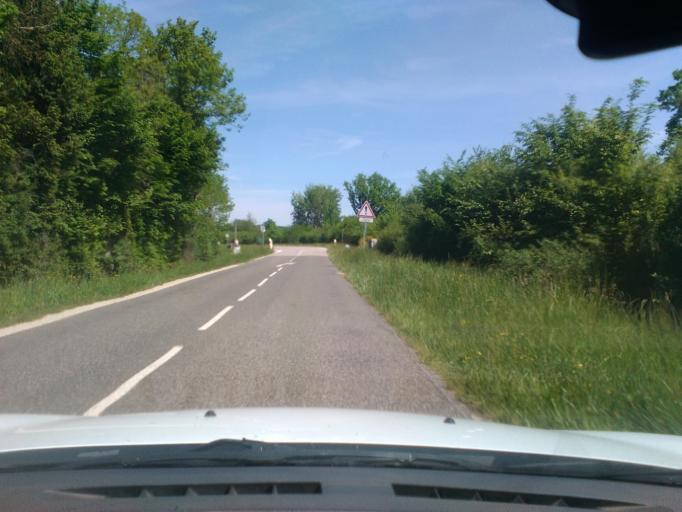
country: FR
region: Lorraine
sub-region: Departement des Vosges
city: Jeanmenil
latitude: 48.3124
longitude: 6.6825
